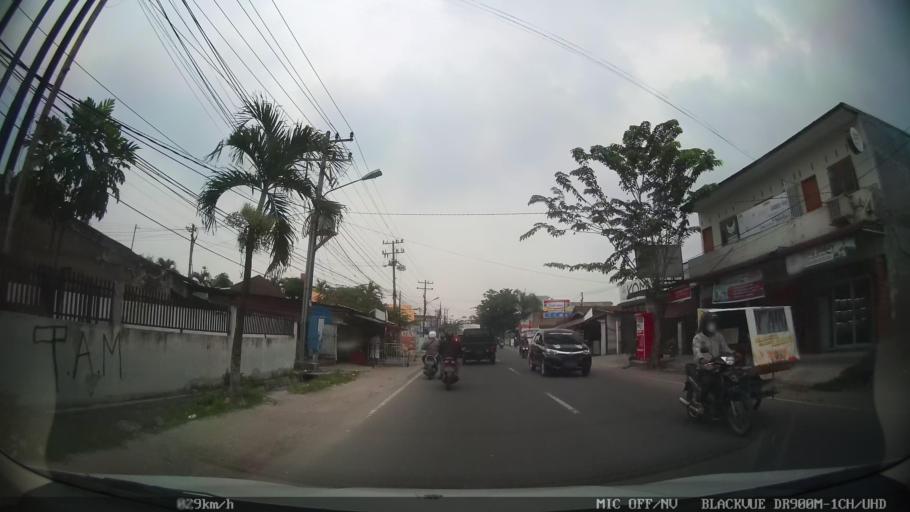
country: ID
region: North Sumatra
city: Deli Tua
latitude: 3.5535
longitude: 98.7162
